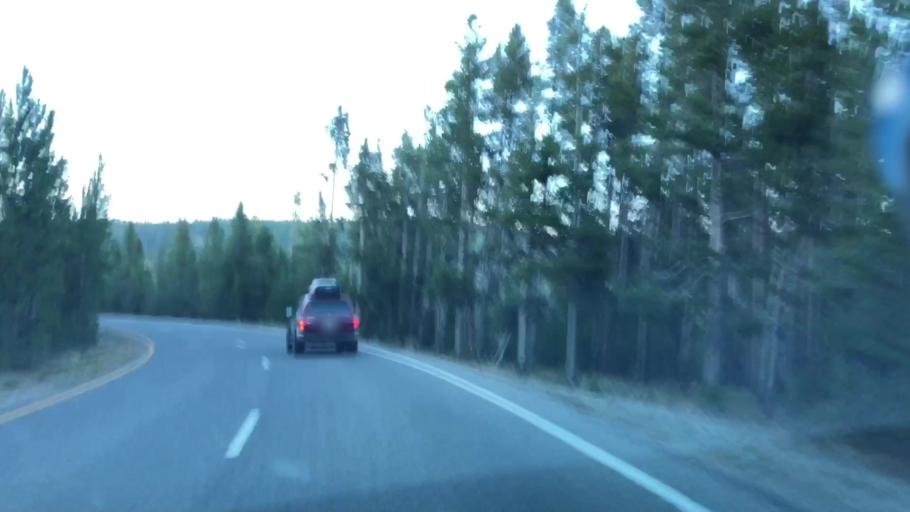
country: US
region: Montana
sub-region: Gallatin County
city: West Yellowstone
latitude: 44.4556
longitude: -110.8233
